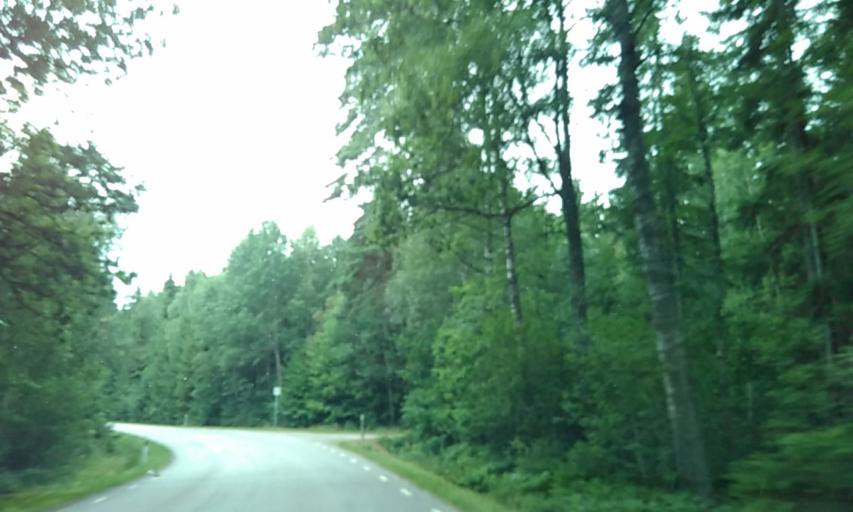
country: SE
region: Vaestra Goetaland
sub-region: Grastorps Kommun
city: Graestorp
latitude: 58.4660
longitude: 12.8079
